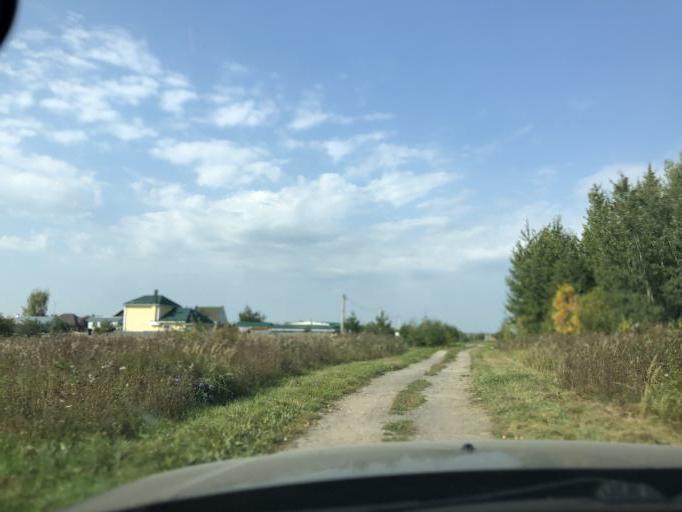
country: RU
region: Moskovskaya
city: L'vovskiy
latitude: 55.3428
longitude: 37.4586
